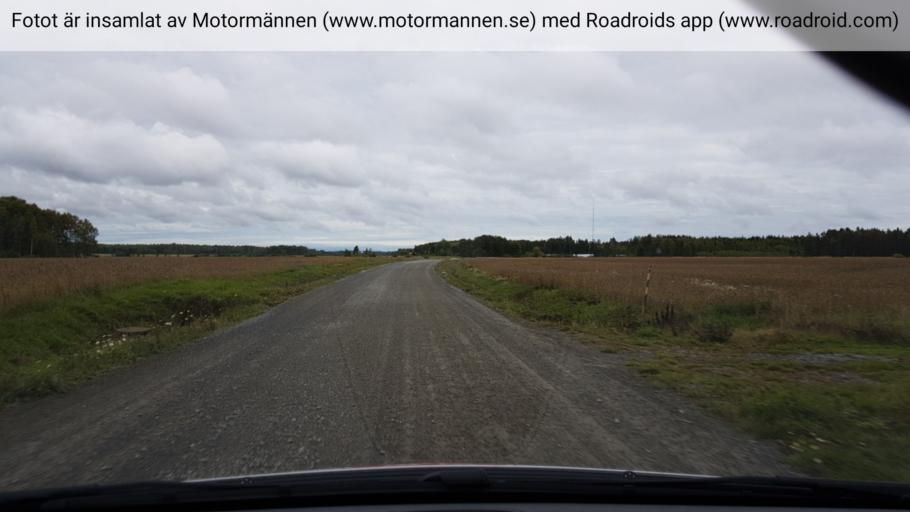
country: SE
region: Vaermland
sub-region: Saffle Kommun
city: Saeffle
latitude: 59.0656
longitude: 13.1613
